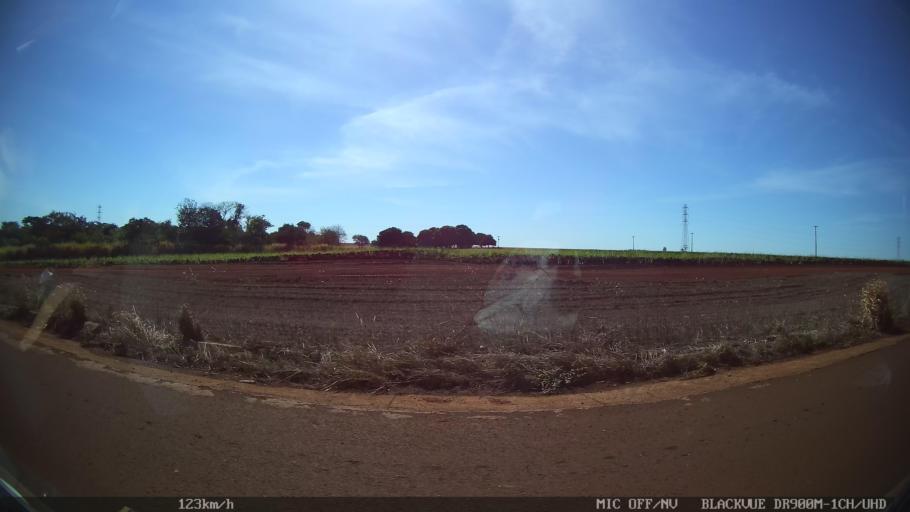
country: BR
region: Sao Paulo
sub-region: Guaira
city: Guaira
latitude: -20.4456
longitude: -48.4078
